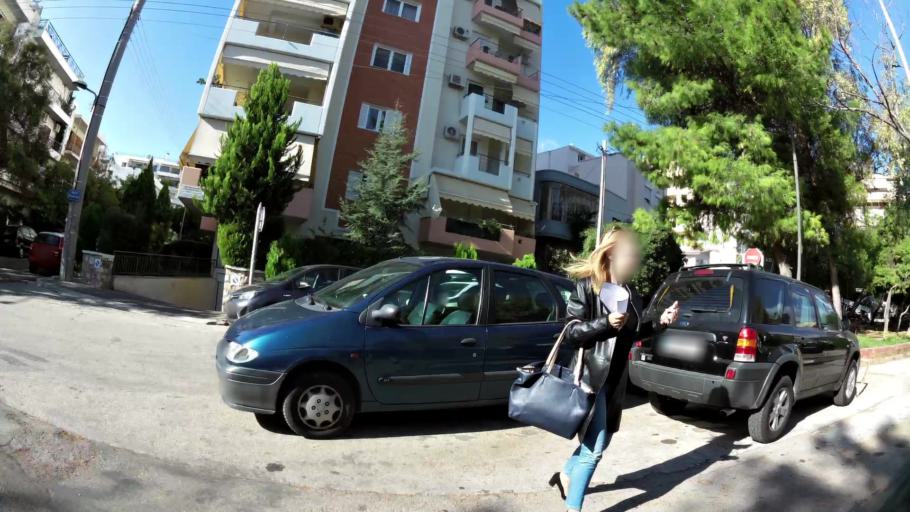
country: GR
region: Attica
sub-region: Nomarchia Athinas
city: Neo Psychiko
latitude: 37.9987
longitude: 23.7780
